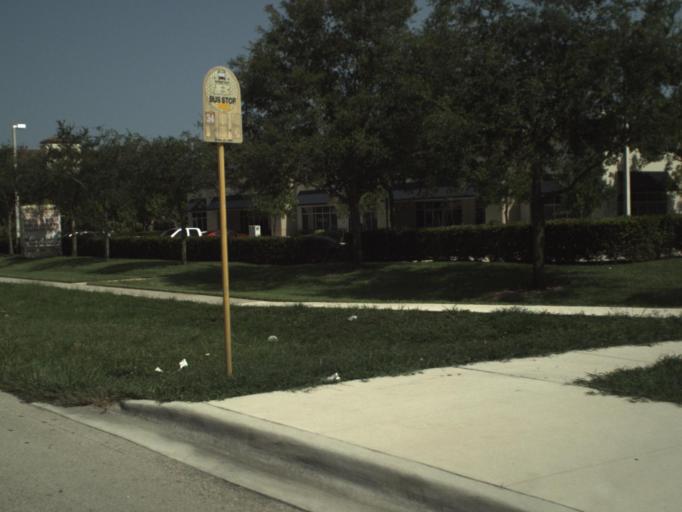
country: US
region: Florida
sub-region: Broward County
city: Coconut Creek
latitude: 26.2743
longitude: -80.1572
